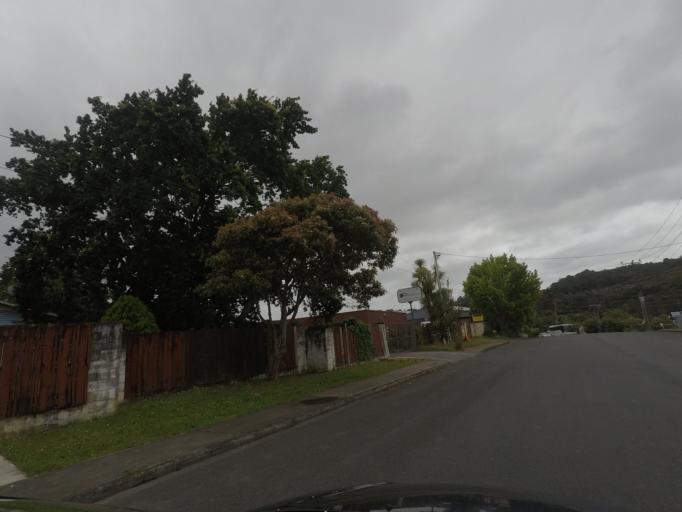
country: NZ
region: Auckland
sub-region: Auckland
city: Waitakere
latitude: -36.9075
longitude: 174.6373
